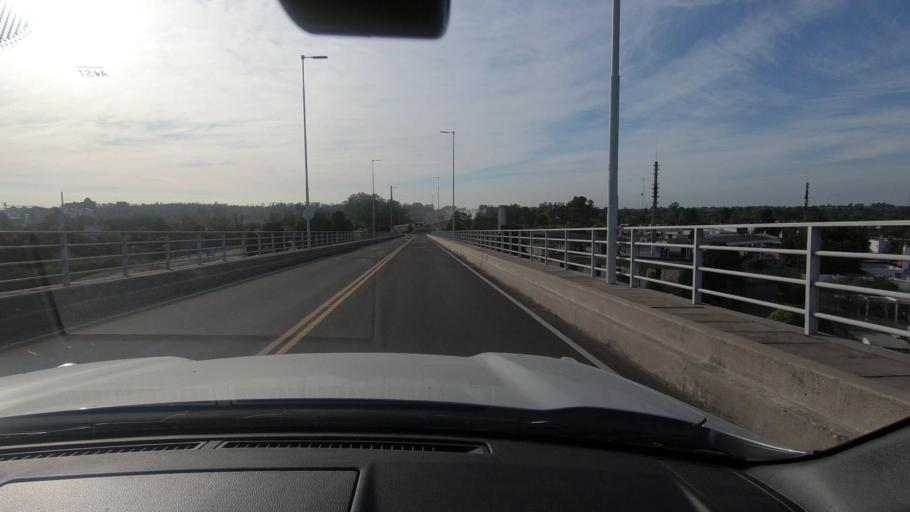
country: AR
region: Entre Rios
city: Colon
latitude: -32.2443
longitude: -58.1497
